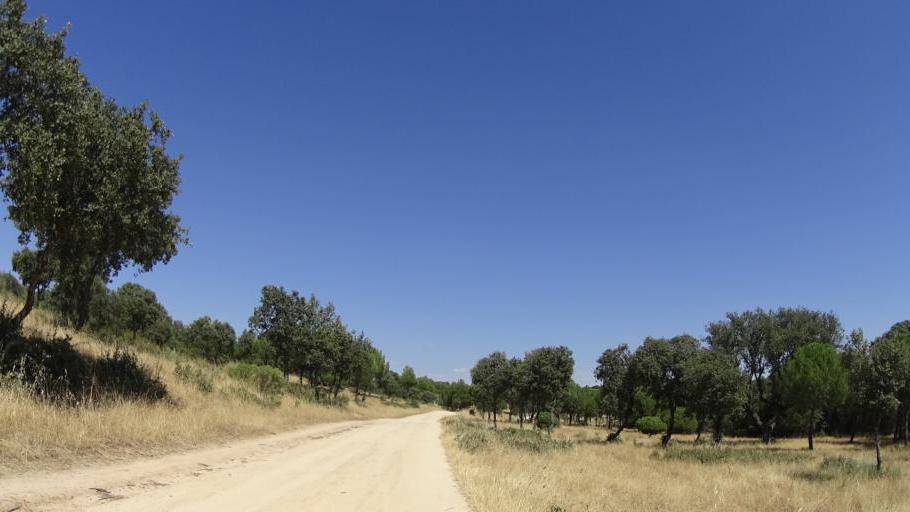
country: ES
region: Madrid
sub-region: Provincia de Madrid
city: Boadilla del Monte
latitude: 40.4300
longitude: -3.8550
